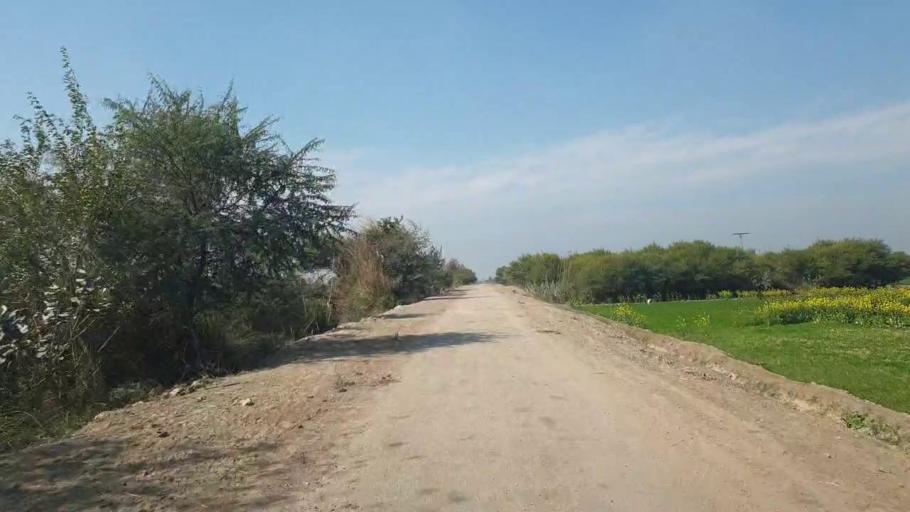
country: PK
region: Sindh
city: Shahdadpur
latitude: 25.9921
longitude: 68.5312
